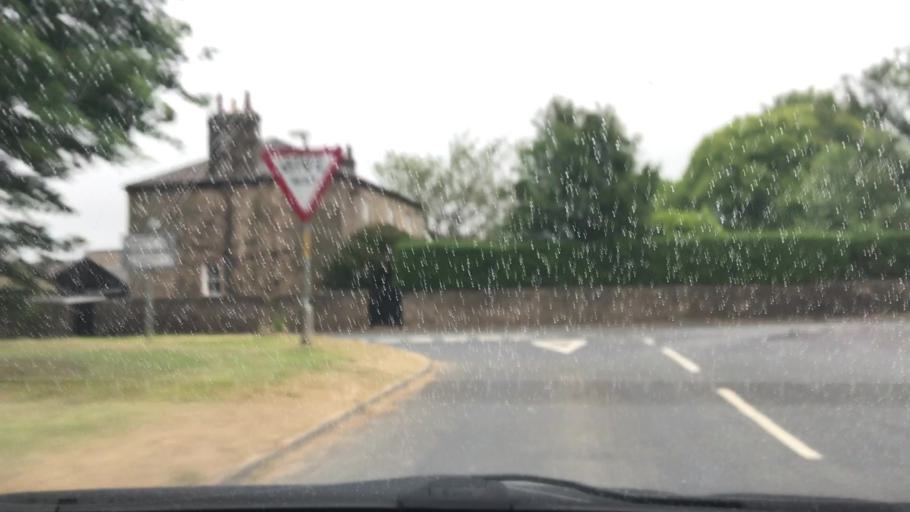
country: GB
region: England
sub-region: City and Borough of Leeds
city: Wetherby
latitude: 53.9595
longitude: -1.4058
